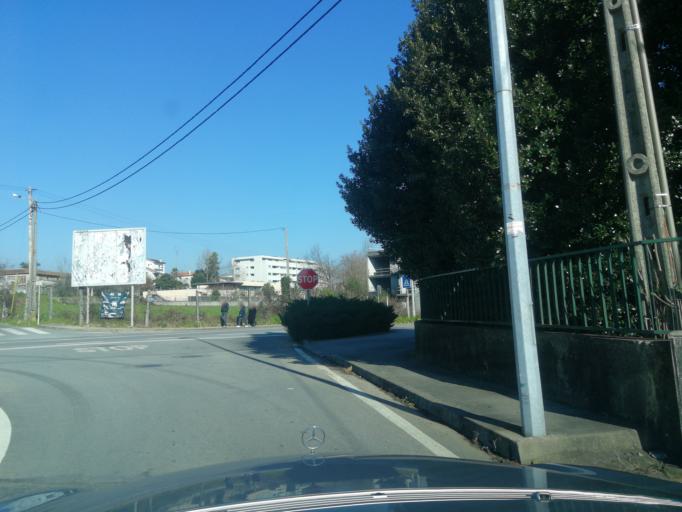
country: PT
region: Braga
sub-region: Guimaraes
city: Ponte
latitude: 41.4881
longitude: -8.3482
